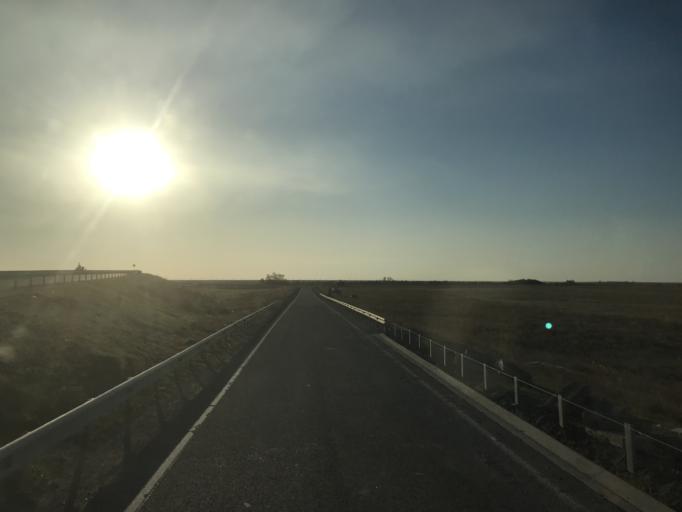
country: KZ
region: Pavlodar
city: Leninskiy
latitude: 52.1556
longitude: 76.8266
